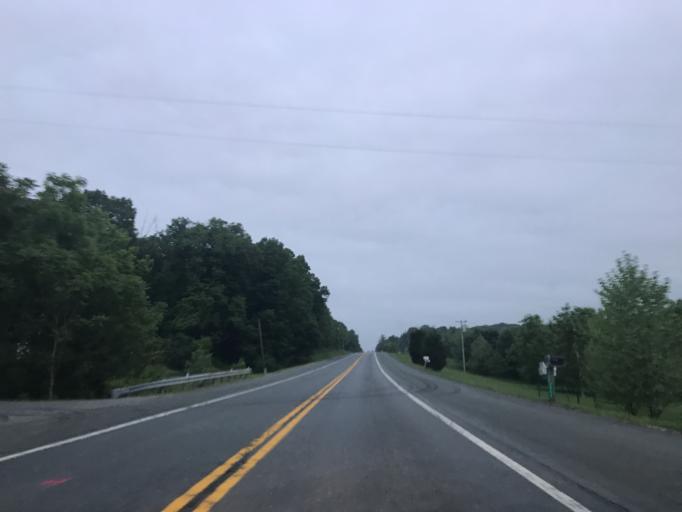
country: US
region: Maryland
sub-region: Frederick County
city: Linganore
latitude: 39.4439
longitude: -77.2494
